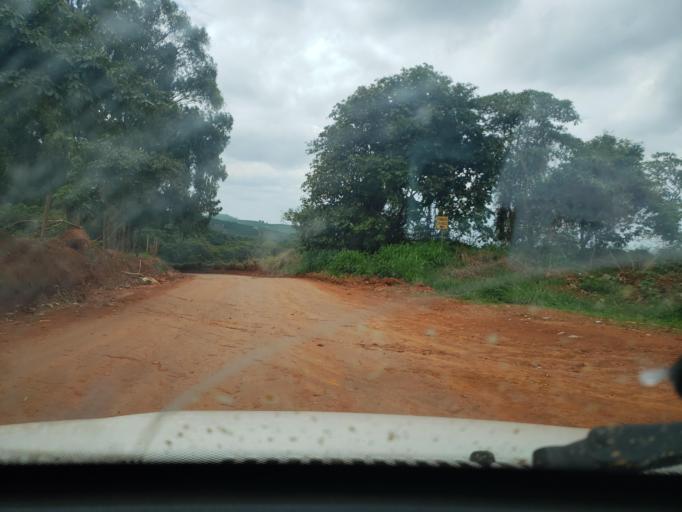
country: BR
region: Minas Gerais
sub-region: Boa Esperanca
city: Boa Esperanca
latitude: -20.9841
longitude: -45.5930
